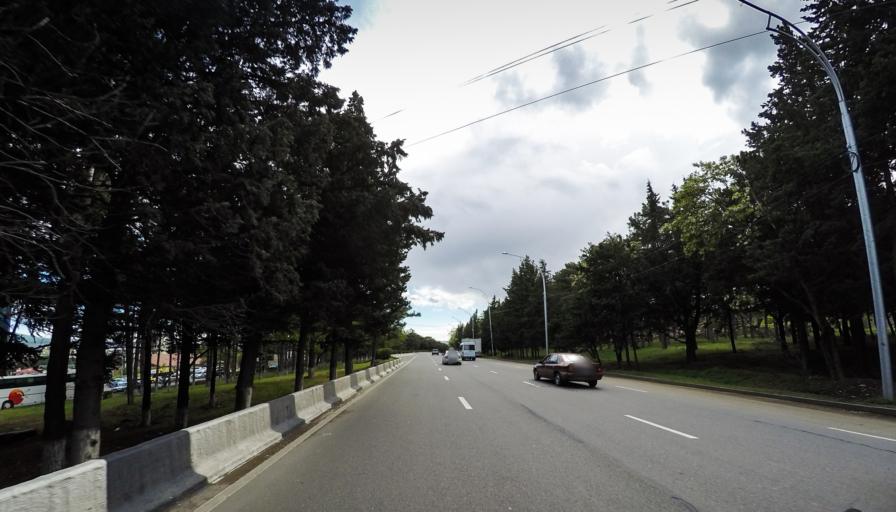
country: GE
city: Zahesi
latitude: 41.8158
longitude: 44.7712
